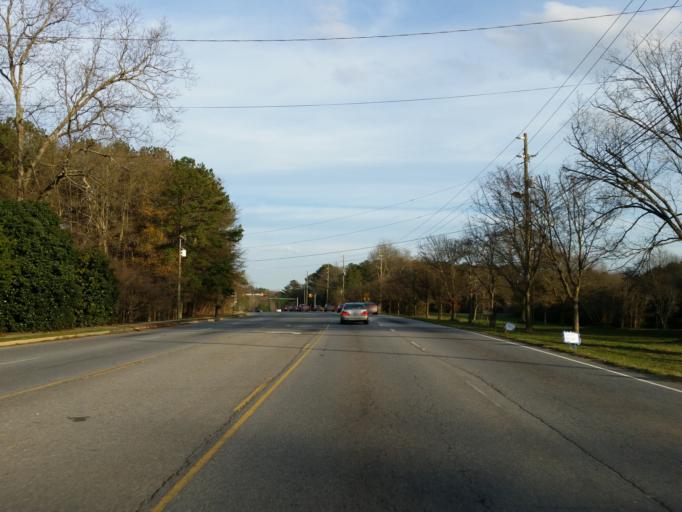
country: US
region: Georgia
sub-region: Cobb County
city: Powder Springs
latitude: 33.8598
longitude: -84.6602
